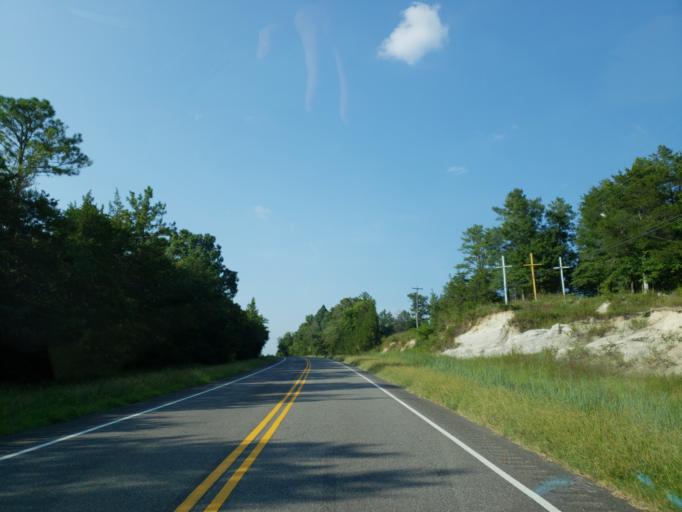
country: US
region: Alabama
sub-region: Sumter County
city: Livingston
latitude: 32.6412
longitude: -88.1717
